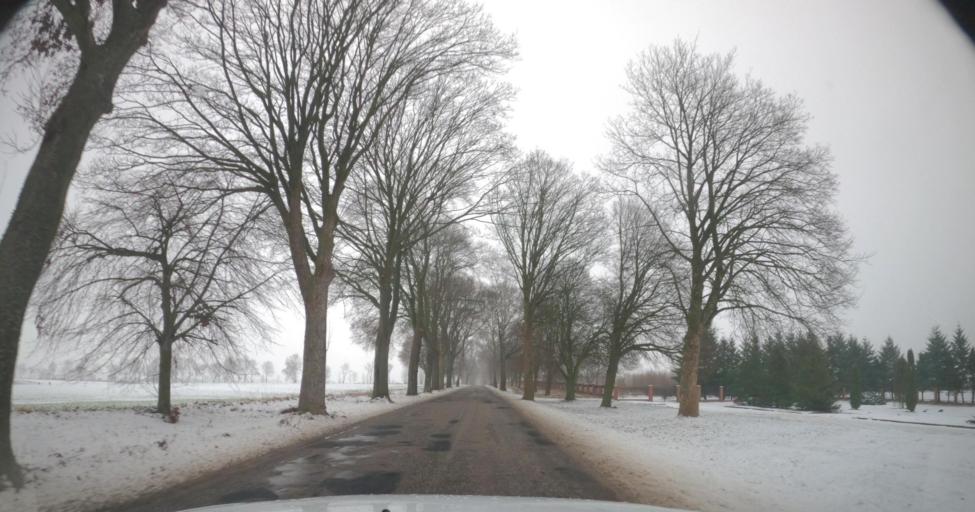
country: PL
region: West Pomeranian Voivodeship
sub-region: Powiat gryficki
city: Gryfice
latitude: 53.9106
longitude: 15.2292
